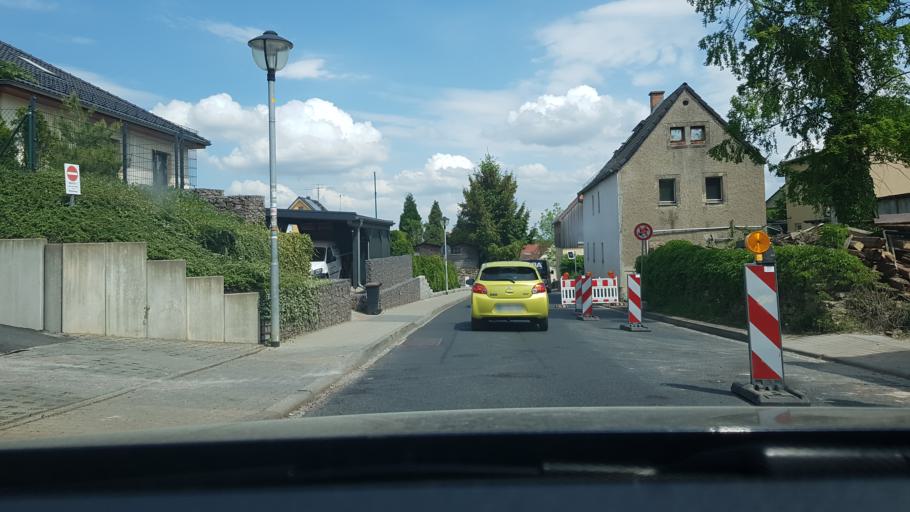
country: DE
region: Saxony
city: Freital
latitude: 51.0293
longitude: 13.6601
